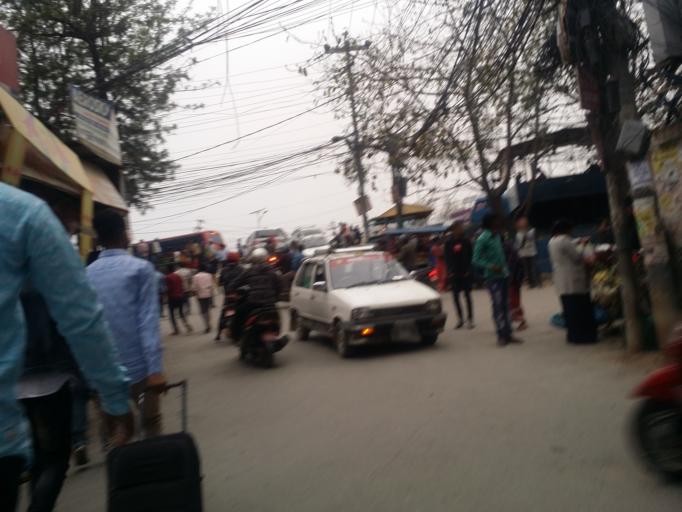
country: NP
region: Central Region
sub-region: Bagmati Zone
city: Kathmandu
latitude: 27.7055
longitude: 85.3476
